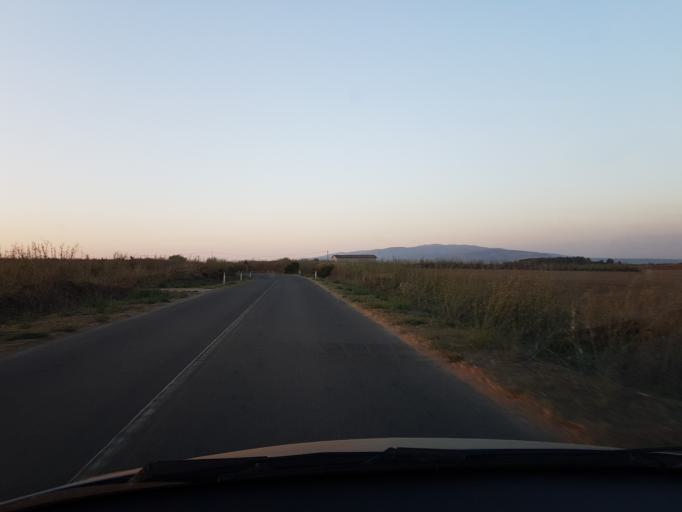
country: IT
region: Sardinia
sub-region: Provincia di Oristano
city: Nurachi
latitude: 39.9769
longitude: 8.4539
